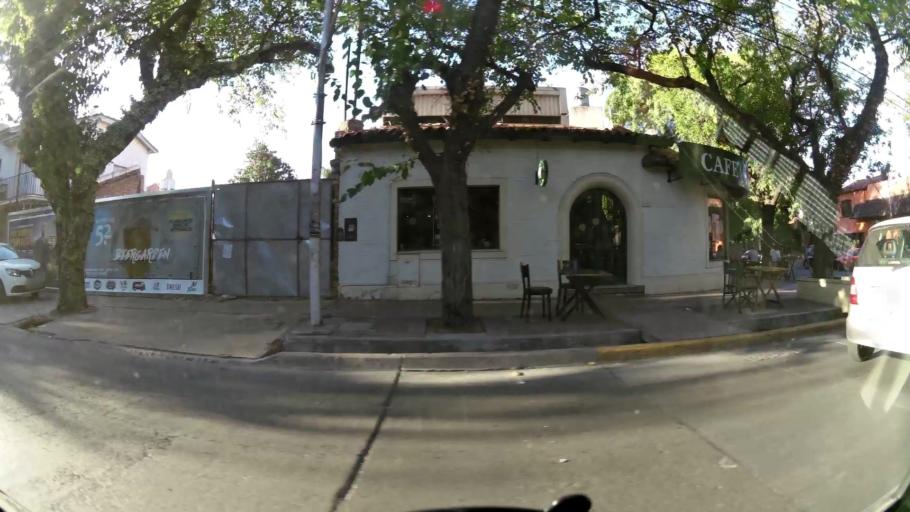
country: AR
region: Mendoza
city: Mendoza
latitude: -32.9037
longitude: -68.8460
